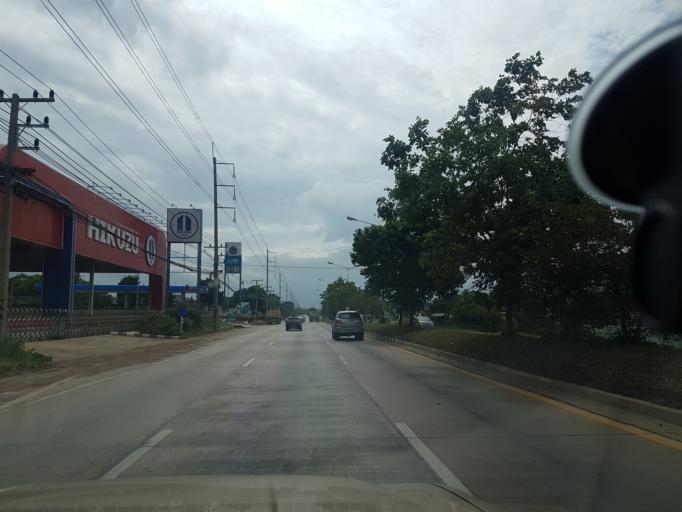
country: TH
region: Sara Buri
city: Phra Phutthabat
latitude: 14.7117
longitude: 100.8281
